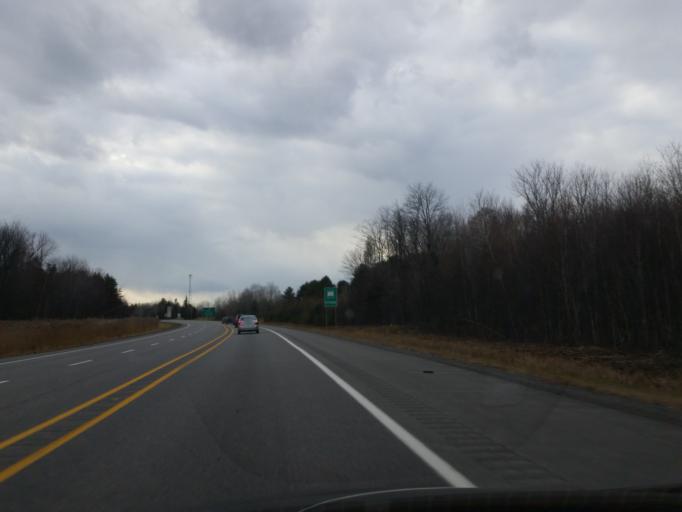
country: CA
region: Quebec
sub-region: Laurentides
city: Saint-Colomban
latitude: 45.6794
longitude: -74.1689
